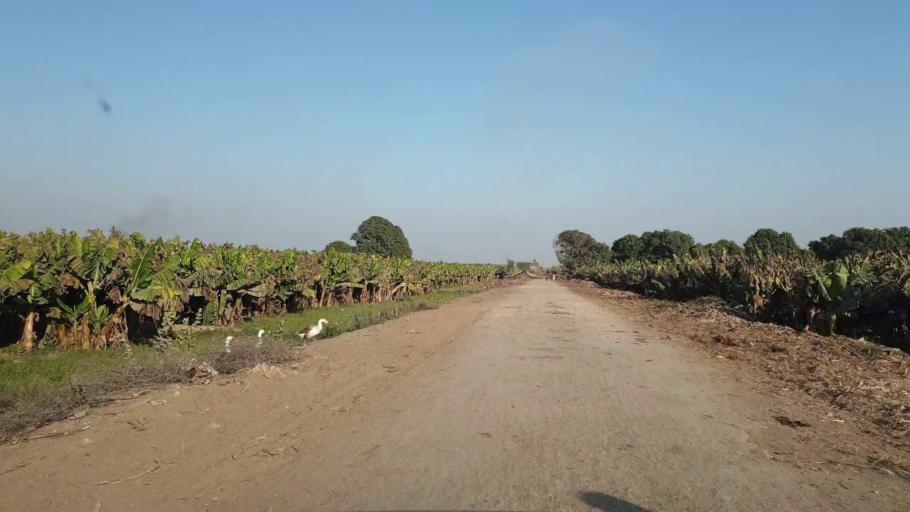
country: PK
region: Sindh
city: Tando Allahyar
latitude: 25.3380
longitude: 68.6882
